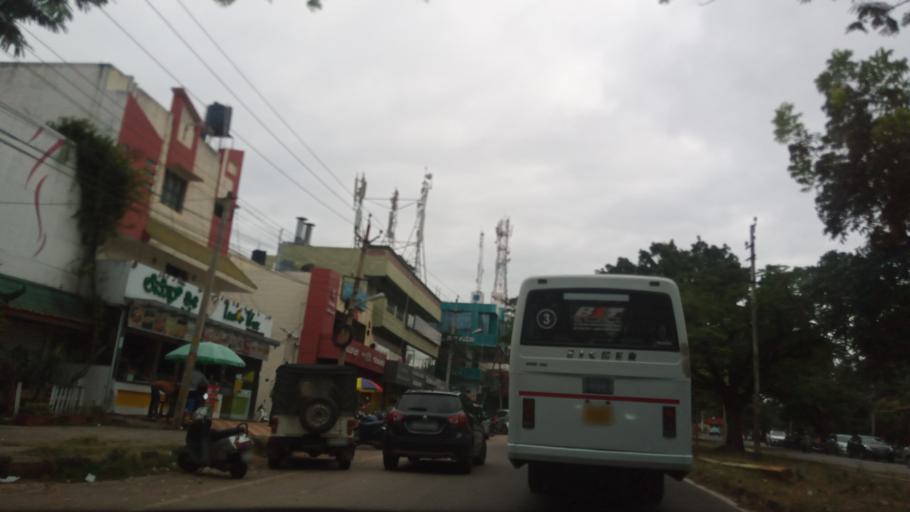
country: IN
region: Karnataka
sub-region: Mysore
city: Mysore
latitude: 12.2949
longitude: 76.6257
